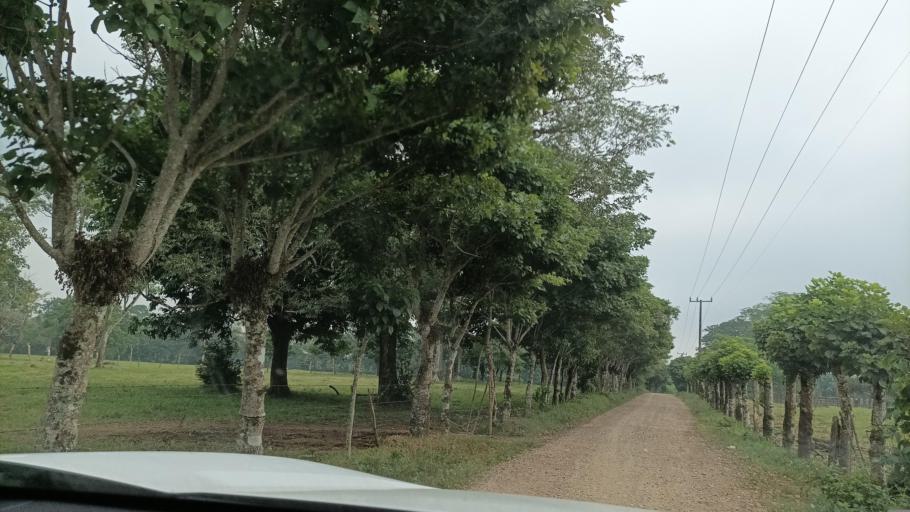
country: MX
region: Veracruz
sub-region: Uxpanapa
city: Poblado 10
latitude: 17.5480
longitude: -94.2298
